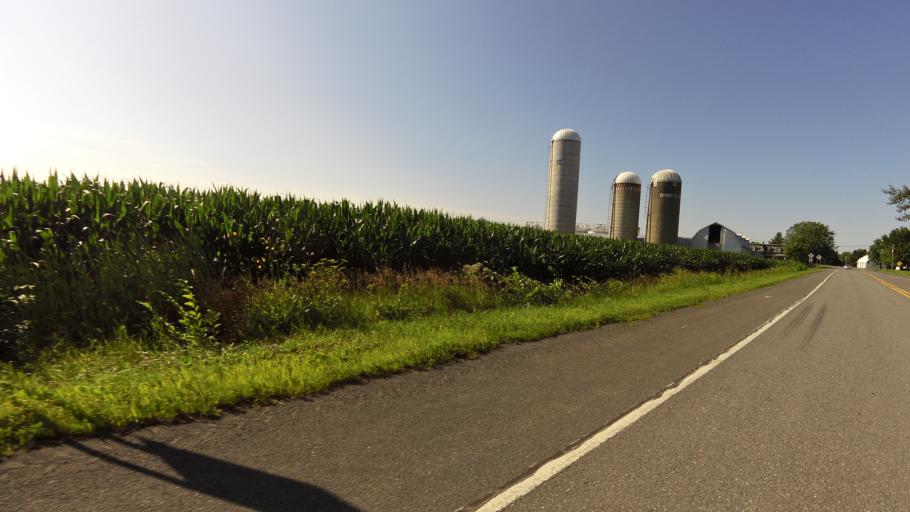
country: CA
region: Quebec
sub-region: Monteregie
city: Napierville
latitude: 45.2797
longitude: -73.3616
